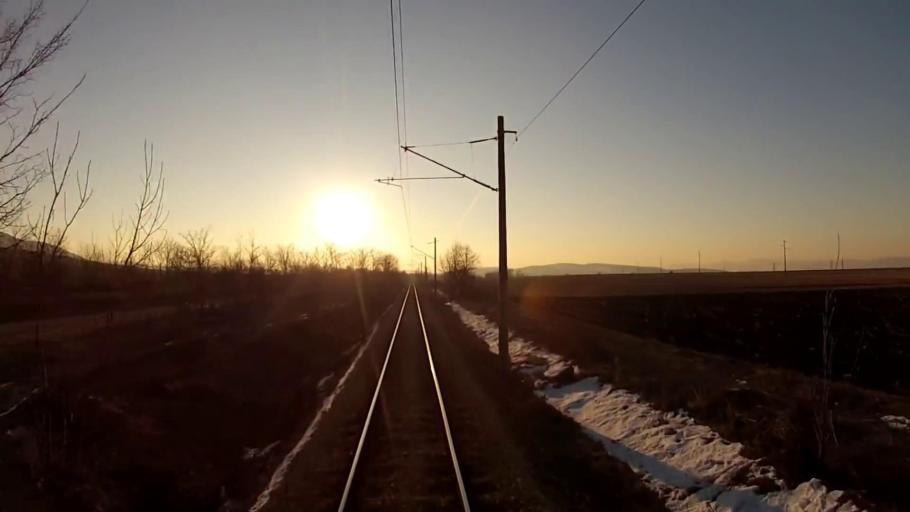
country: BG
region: Sofiya
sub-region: Obshtina Dragoman
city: Dragoman
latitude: 42.8902
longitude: 22.9749
